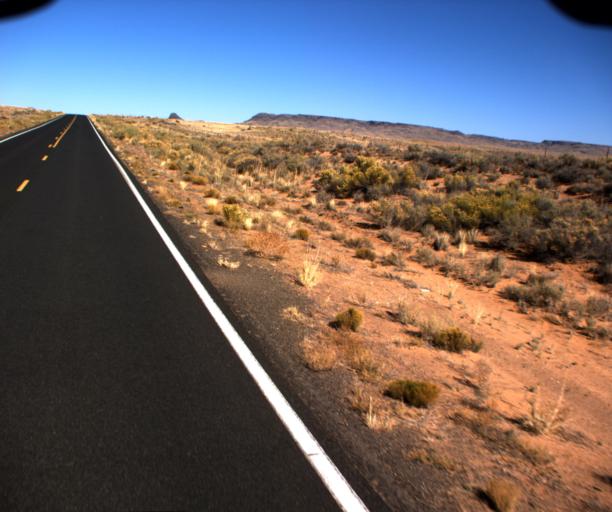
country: US
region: Arizona
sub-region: Navajo County
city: Dilkon
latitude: 35.3605
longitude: -110.4246
